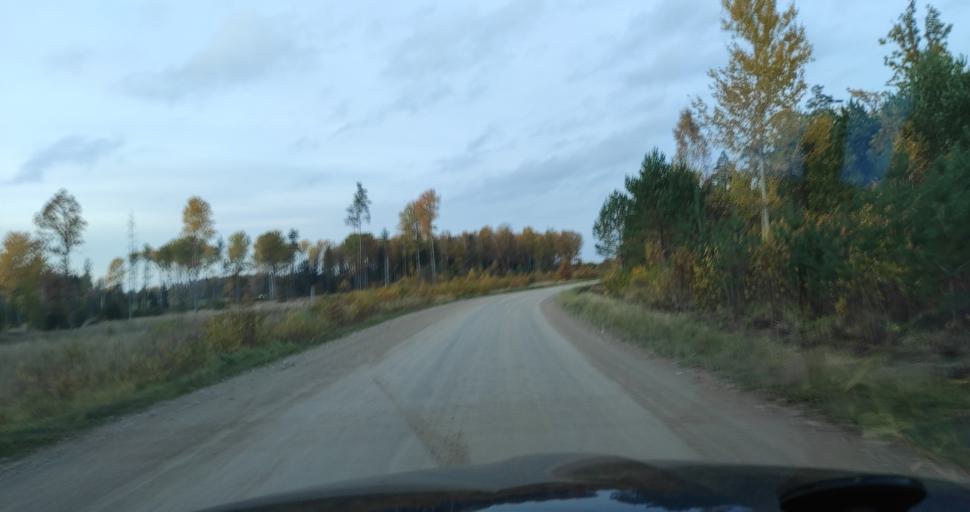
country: LV
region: Aizpute
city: Aizpute
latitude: 56.6727
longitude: 21.7913
